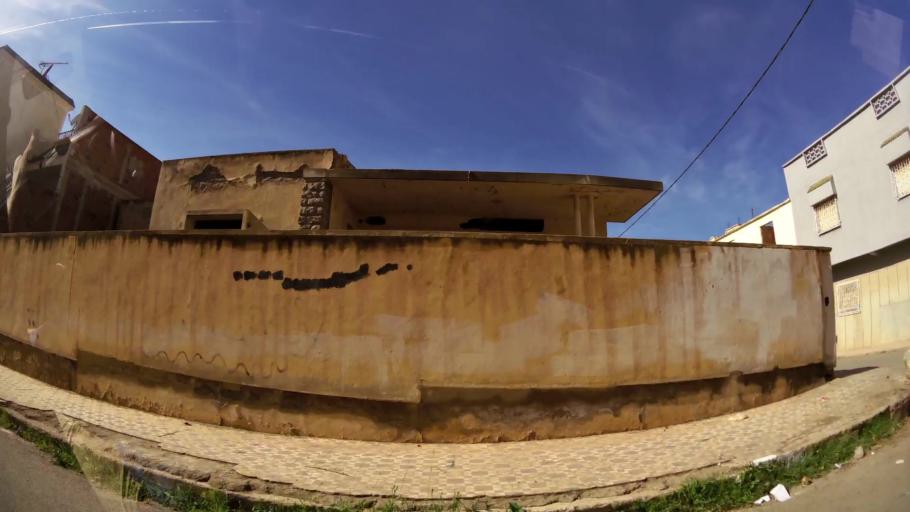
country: MA
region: Oriental
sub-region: Oujda-Angad
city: Oujda
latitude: 34.6692
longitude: -1.9165
